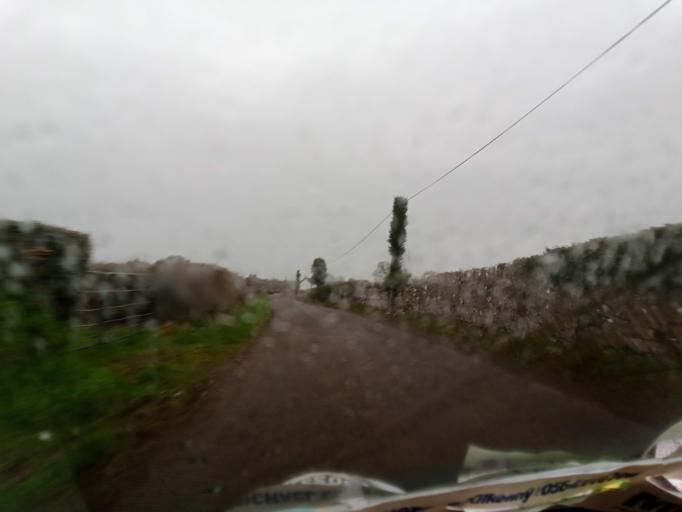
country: IE
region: Munster
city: Fethard
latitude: 52.5614
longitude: -7.7665
